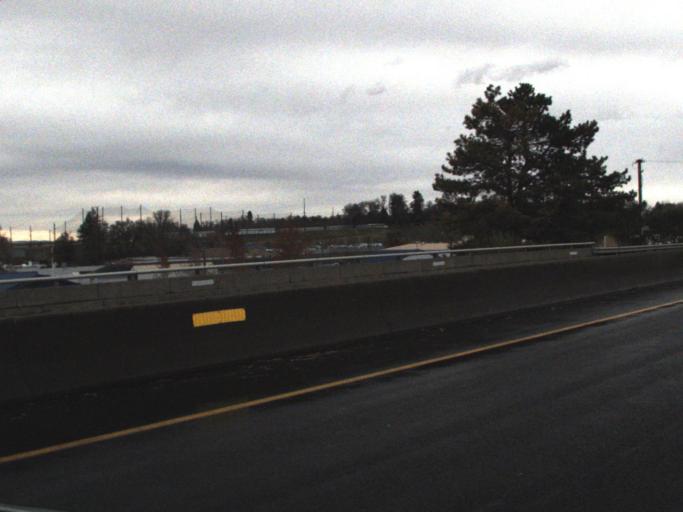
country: US
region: Washington
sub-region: Walla Walla County
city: Walla Walla
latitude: 46.0727
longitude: -118.3427
